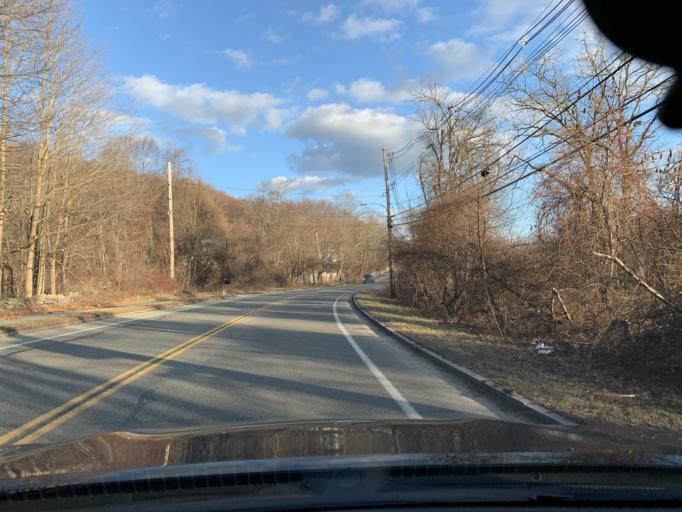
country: US
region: Massachusetts
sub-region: Essex County
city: Middleton
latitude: 42.5963
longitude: -70.9901
